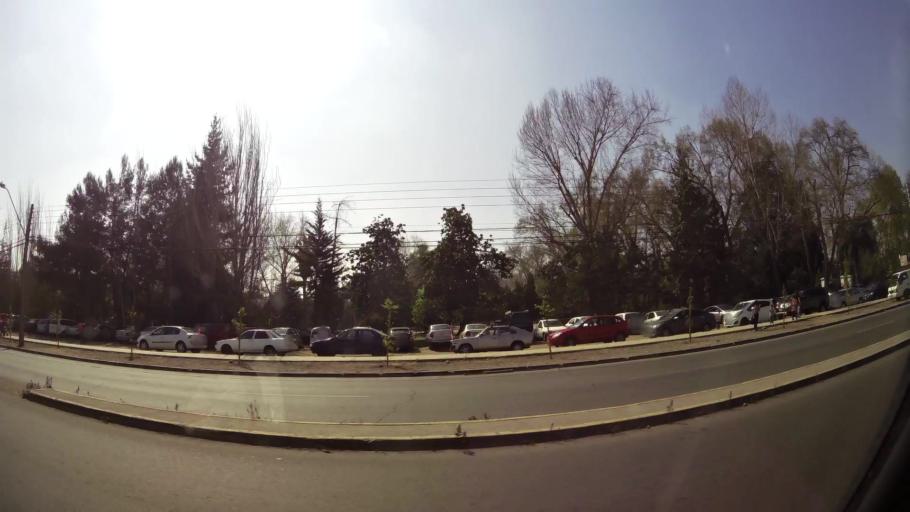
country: CL
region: Santiago Metropolitan
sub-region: Provincia de Santiago
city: Santiago
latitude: -33.4442
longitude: -70.6846
